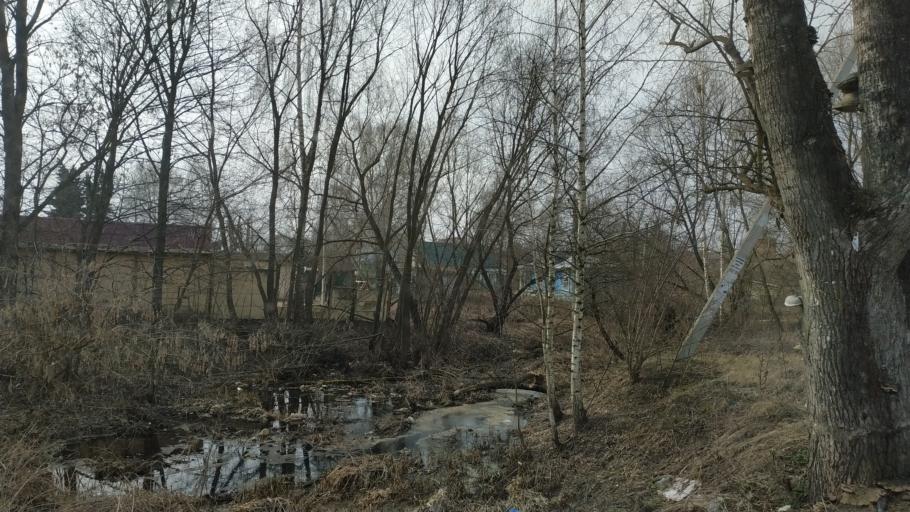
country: RU
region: Moskovskaya
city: Beloozerskiy
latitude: 55.4308
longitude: 38.4976
